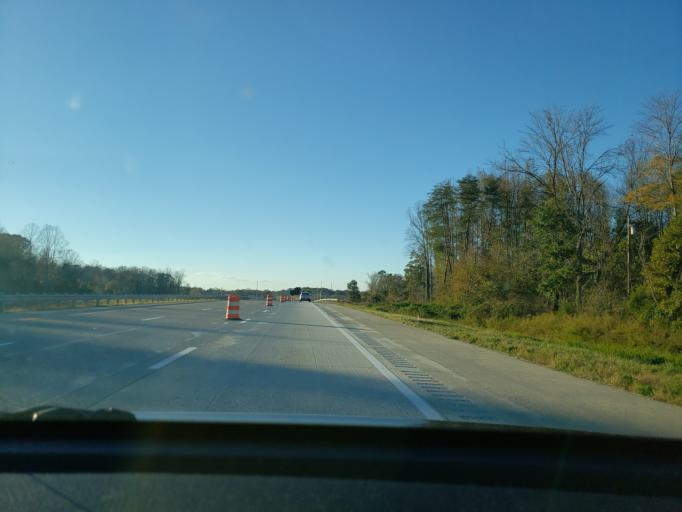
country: US
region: North Carolina
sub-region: Forsyth County
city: Walkertown
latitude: 36.1416
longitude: -80.1471
